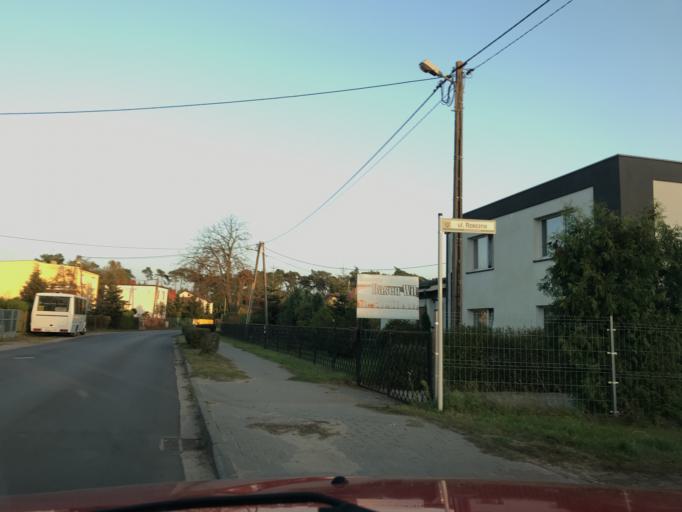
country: PL
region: Greater Poland Voivodeship
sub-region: Powiat poznanski
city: Baranowo
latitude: 52.3900
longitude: 16.7402
